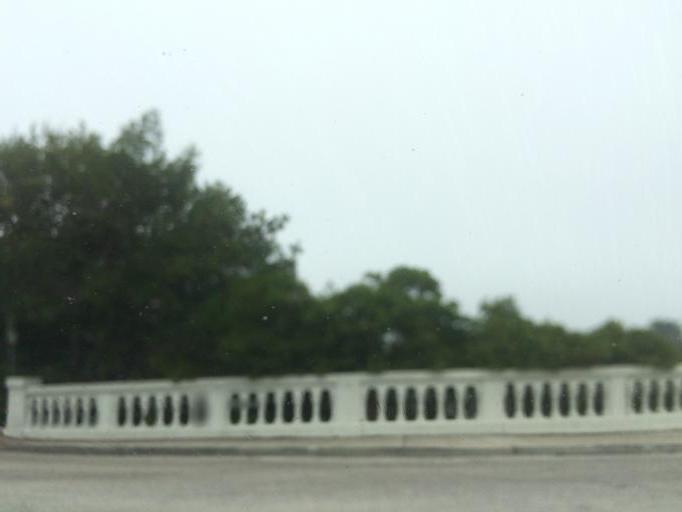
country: US
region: Florida
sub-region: Pinellas County
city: Saint Petersburg
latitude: 27.7921
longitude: -82.6268
